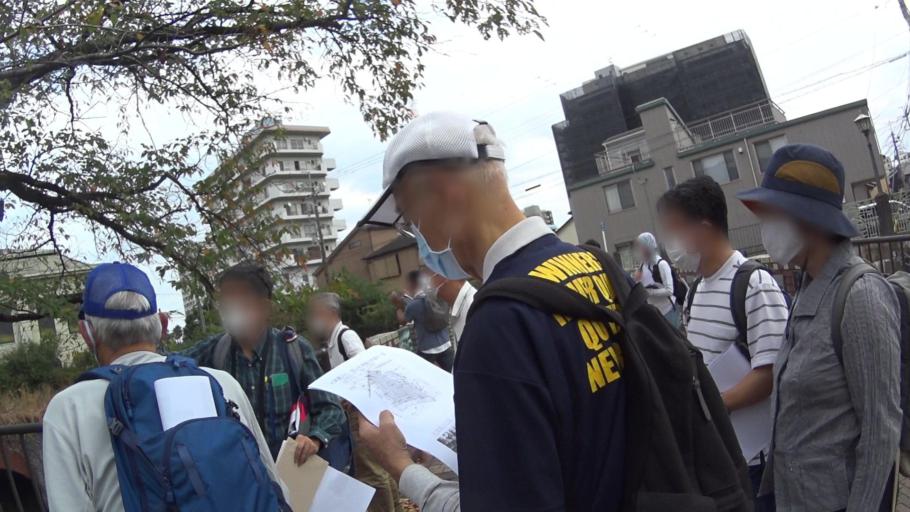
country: JP
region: Osaka
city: Kishiwada
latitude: 34.5141
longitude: 135.3468
